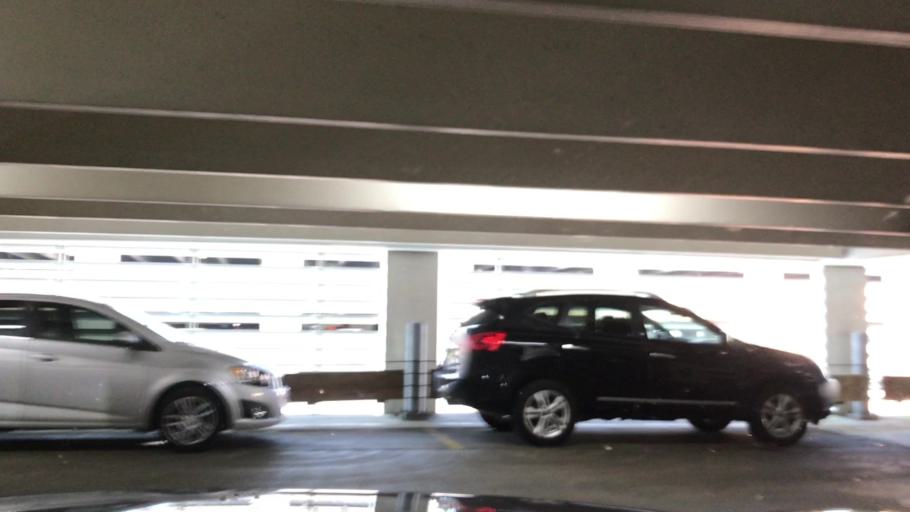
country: US
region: New Jersey
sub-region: Atlantic County
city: Atlantic City
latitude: 39.3608
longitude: -74.4402
